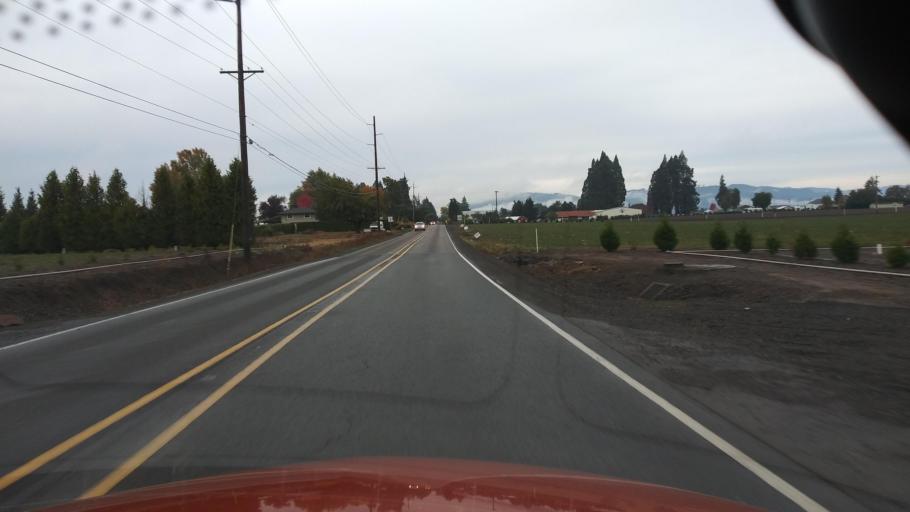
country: US
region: Oregon
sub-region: Washington County
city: Cornelius
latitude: 45.5512
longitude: -123.0774
